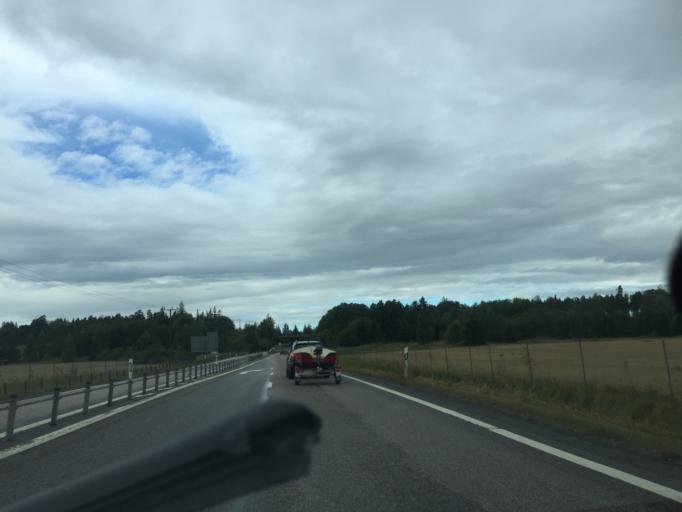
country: SE
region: Soedermanland
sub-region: Eskilstuna Kommun
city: Hallbybrunn
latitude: 59.3960
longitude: 16.4476
